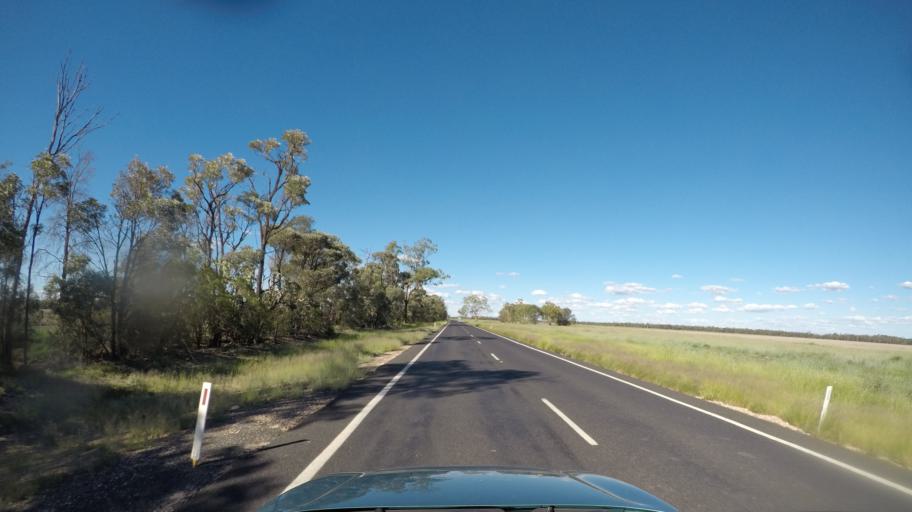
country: AU
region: Queensland
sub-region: Goondiwindi
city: Goondiwindi
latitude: -28.1418
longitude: 150.6904
